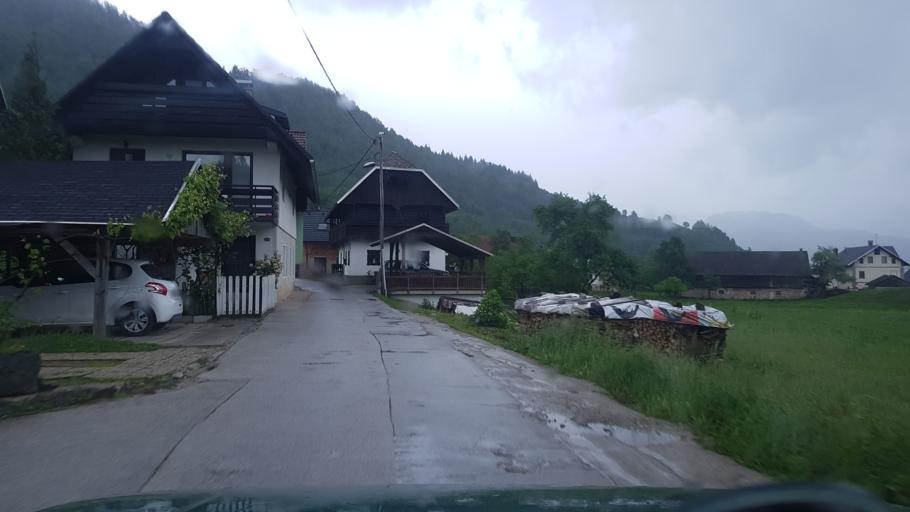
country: SI
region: Bled
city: Zasip
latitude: 46.3872
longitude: 14.0892
